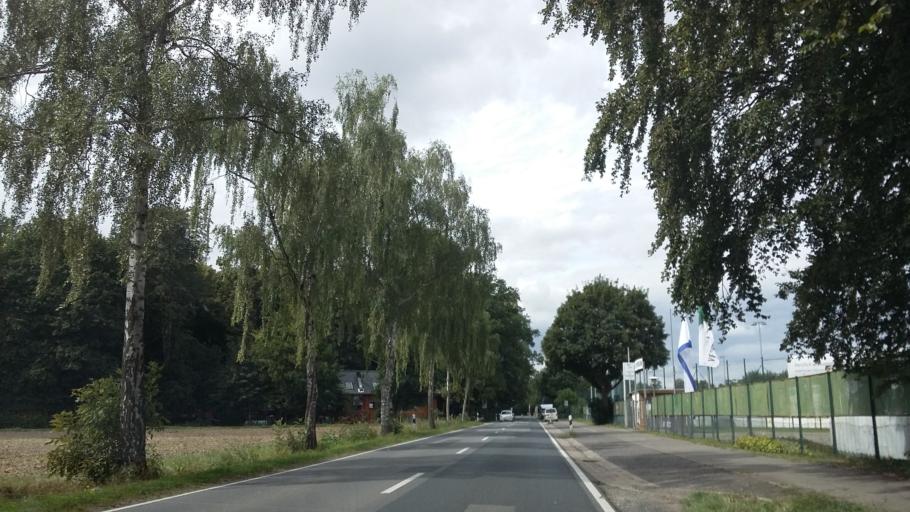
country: DE
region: Lower Saxony
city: Harsum
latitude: 52.2140
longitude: 9.9455
